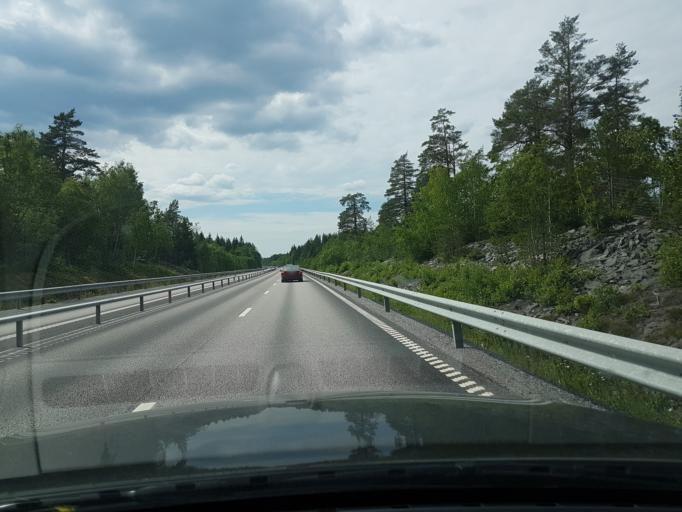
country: SE
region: Stockholm
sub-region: Norrtalje Kommun
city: Norrtalje
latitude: 59.7351
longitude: 18.7770
